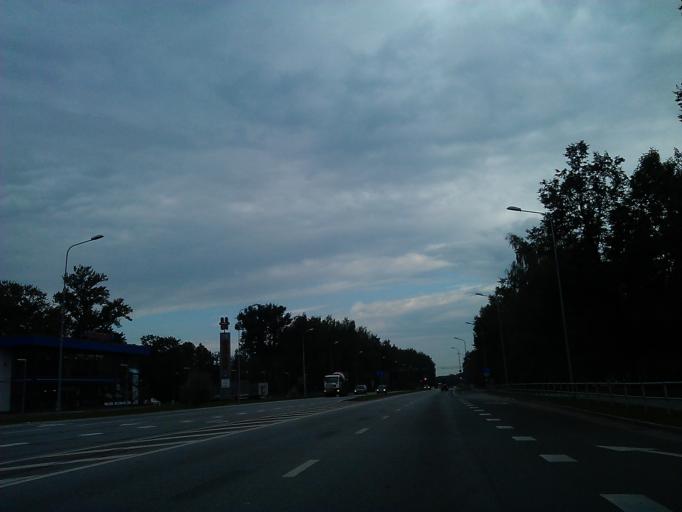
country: LV
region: Salaspils
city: Salaspils
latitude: 56.8518
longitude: 24.3347
